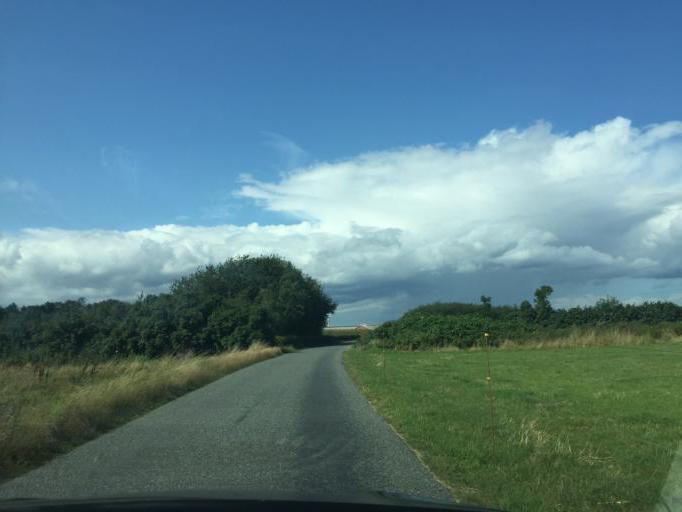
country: DK
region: South Denmark
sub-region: Faaborg-Midtfyn Kommune
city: Arslev
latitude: 55.3241
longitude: 10.4882
